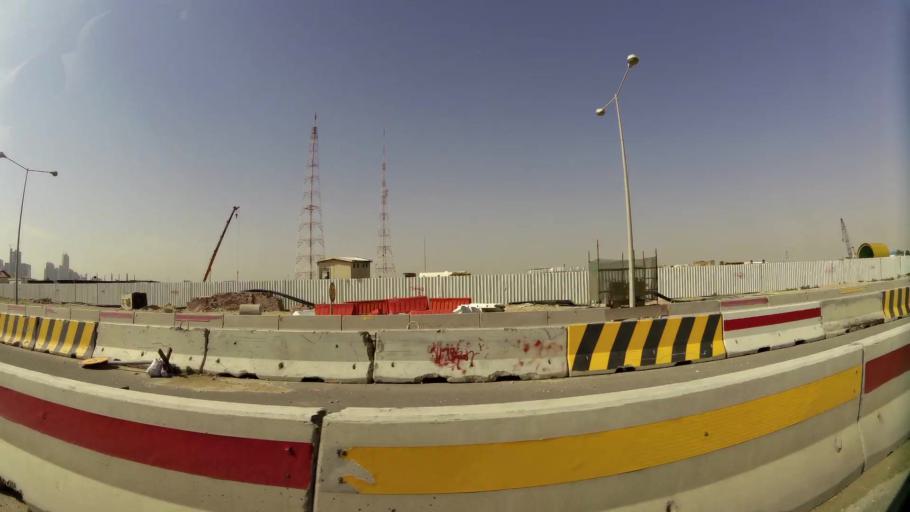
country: QA
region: Baladiyat ad Dawhah
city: Doha
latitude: 25.3382
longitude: 51.5144
